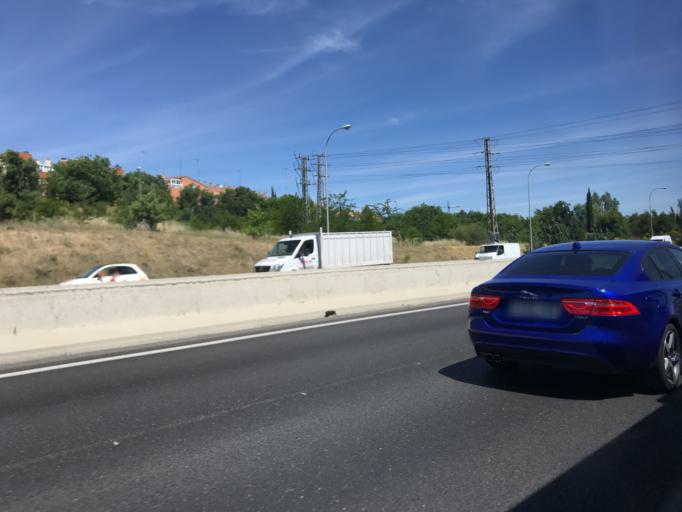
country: ES
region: Madrid
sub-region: Provincia de Madrid
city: San Blas
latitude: 40.4252
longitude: -3.5984
